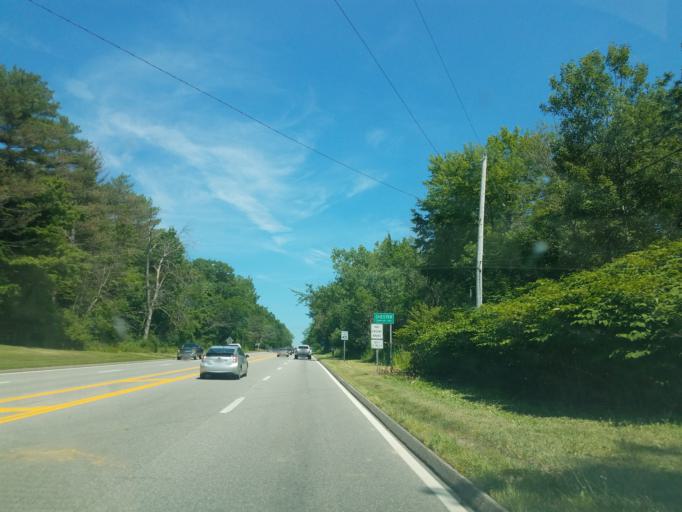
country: US
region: Ohio
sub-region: Cuyahoga County
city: Gates Mills
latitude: 41.5225
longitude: -81.3906
